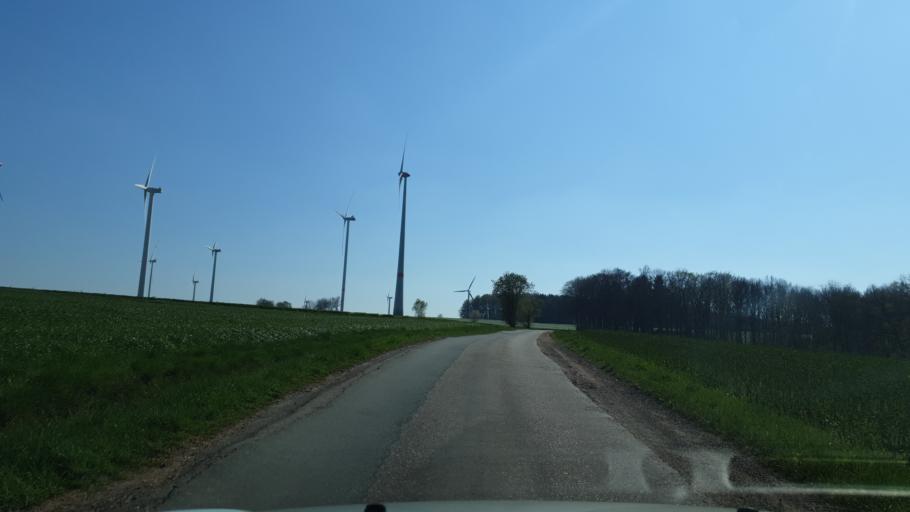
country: DE
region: Saxony
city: Bernsdorf
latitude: 50.7722
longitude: 12.6842
